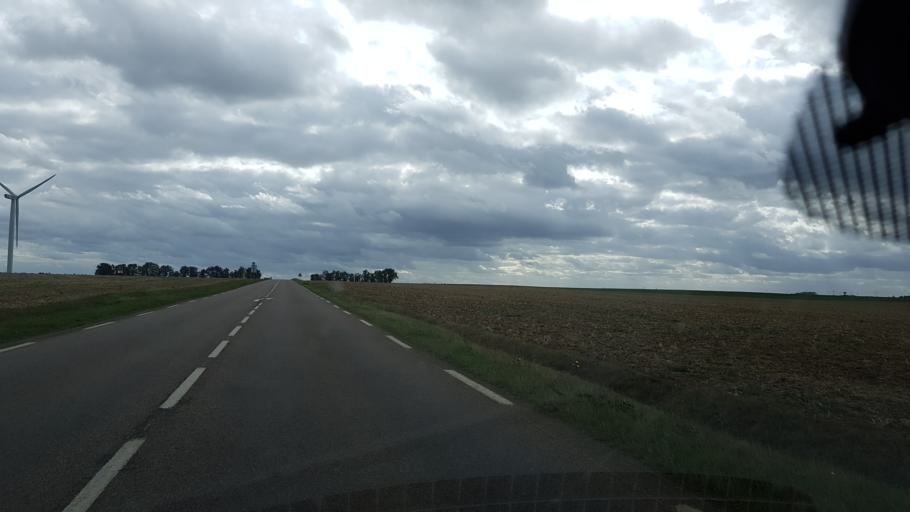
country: FR
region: Ile-de-France
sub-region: Departement de l'Essonne
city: Etampes
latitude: 48.3994
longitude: 2.1743
